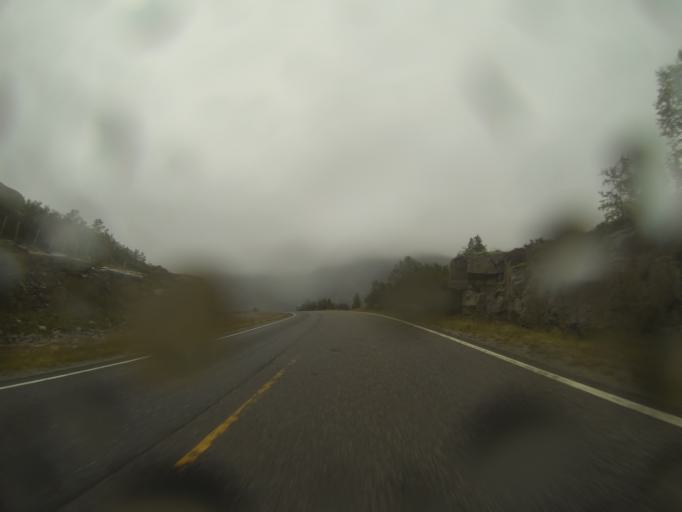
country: NO
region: Vest-Agder
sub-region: Sirdal
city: Tonstad
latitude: 58.9130
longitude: 6.7467
